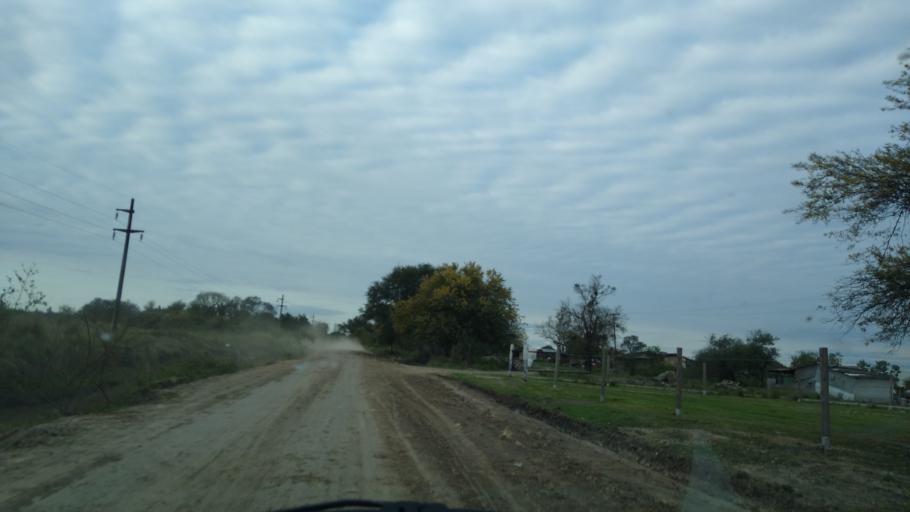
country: AR
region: Chaco
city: Fontana
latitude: -27.3843
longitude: -59.0429
